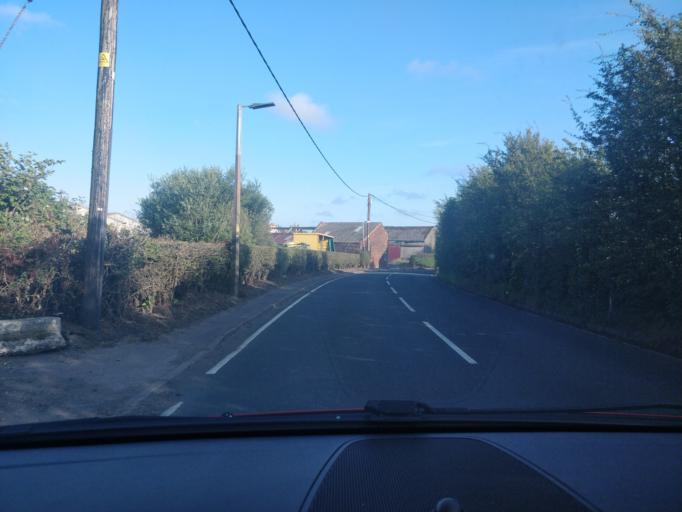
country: GB
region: England
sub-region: Lancashire
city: Tarleton
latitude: 53.6434
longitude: -2.8511
